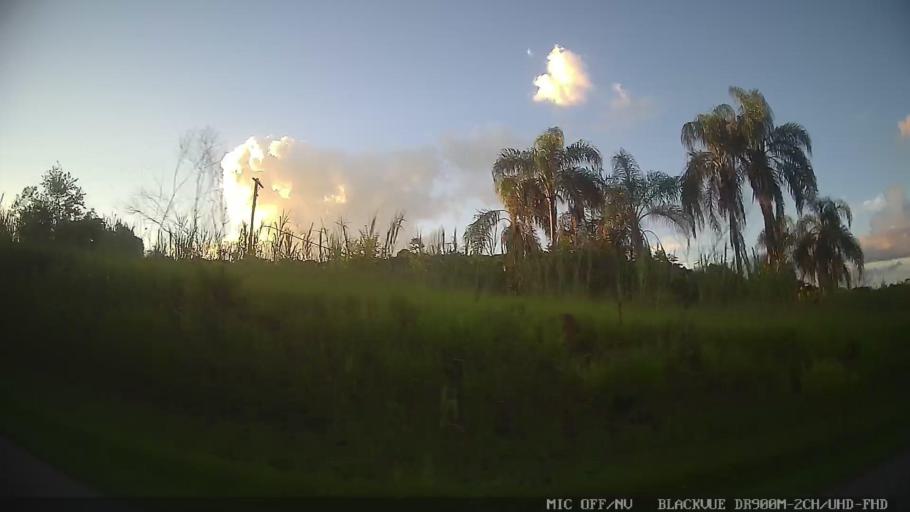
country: BR
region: Sao Paulo
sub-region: Jarinu
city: Jarinu
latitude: -23.0210
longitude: -46.7495
